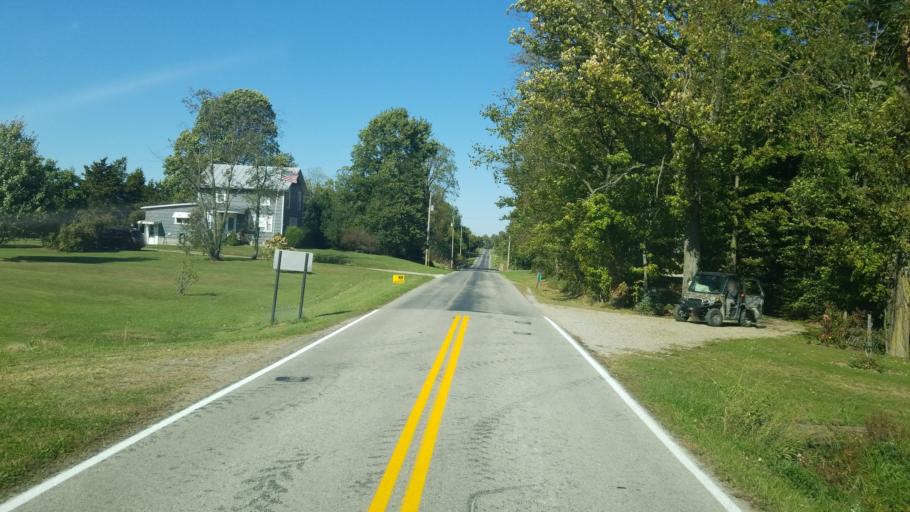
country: US
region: Ohio
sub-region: Huron County
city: Greenwich
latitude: 41.0418
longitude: -82.5112
